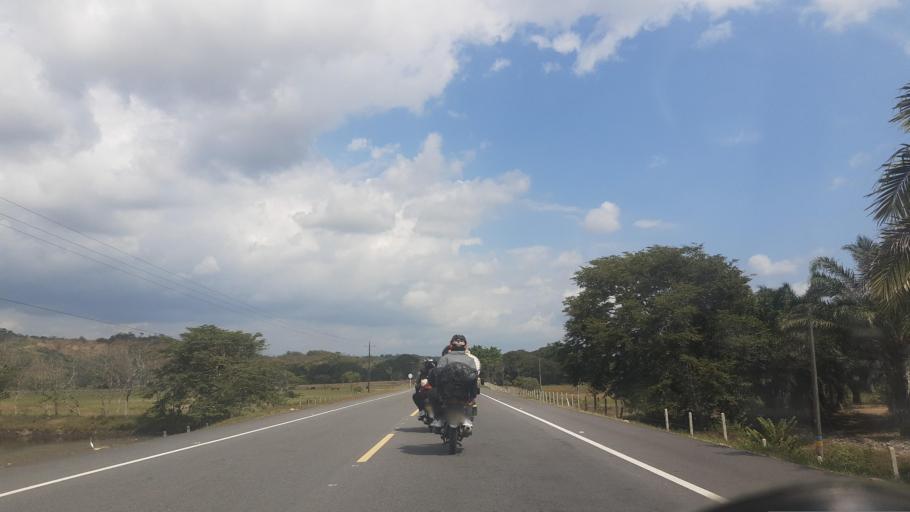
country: CO
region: Casanare
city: Tauramena
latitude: 4.9216
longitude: -72.6741
